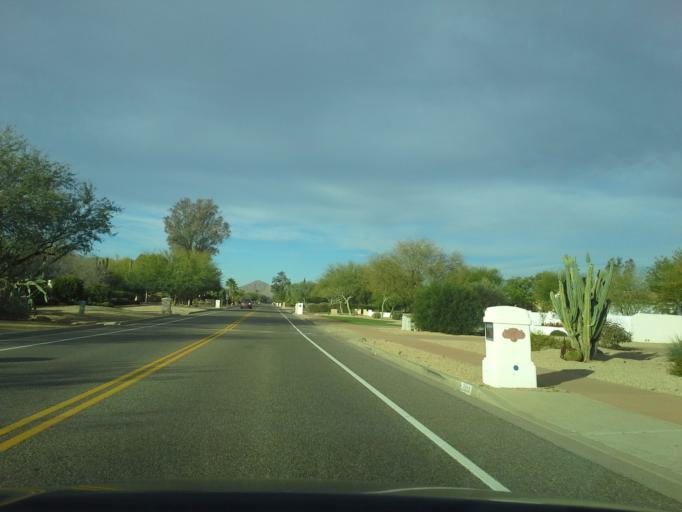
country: US
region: Arizona
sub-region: Maricopa County
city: Paradise Valley
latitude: 33.5675
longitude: -111.9298
